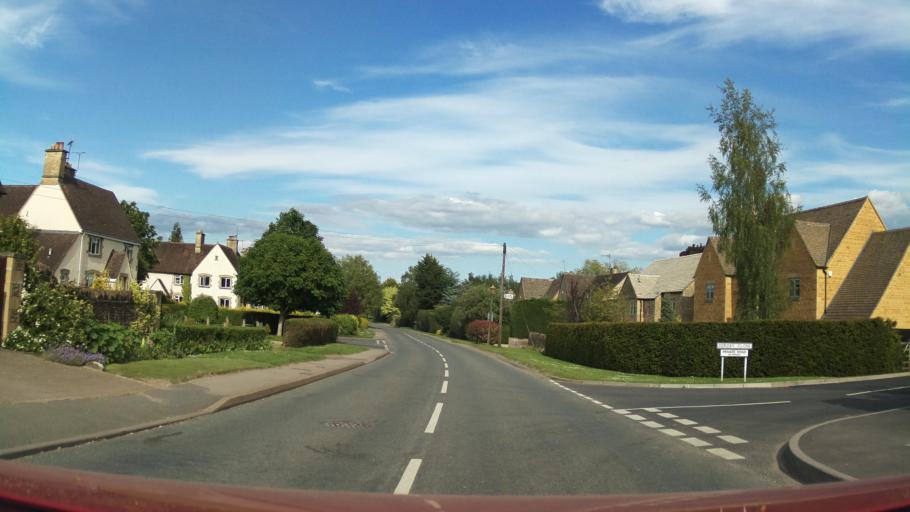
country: GB
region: England
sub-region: Gloucestershire
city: Chipping Campden
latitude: 52.0524
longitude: -1.7685
